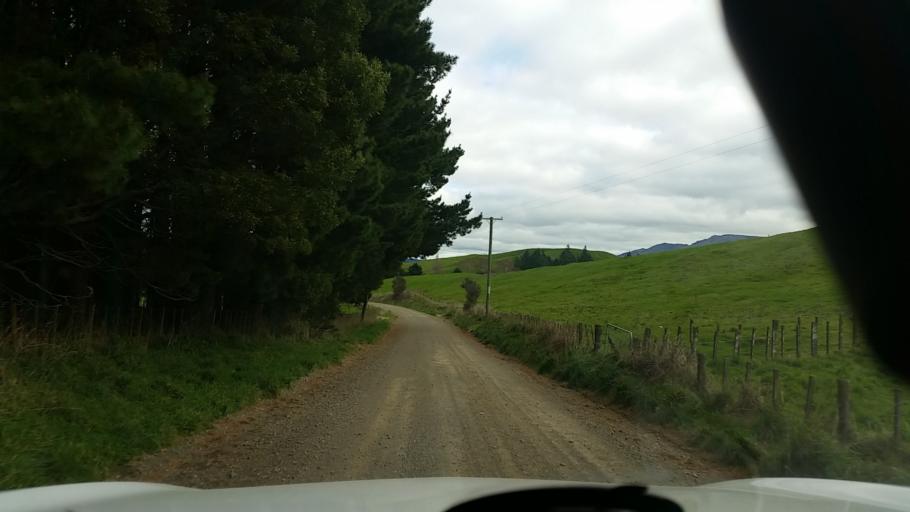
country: NZ
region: Hawke's Bay
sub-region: Napier City
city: Napier
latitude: -39.1811
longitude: 176.8542
